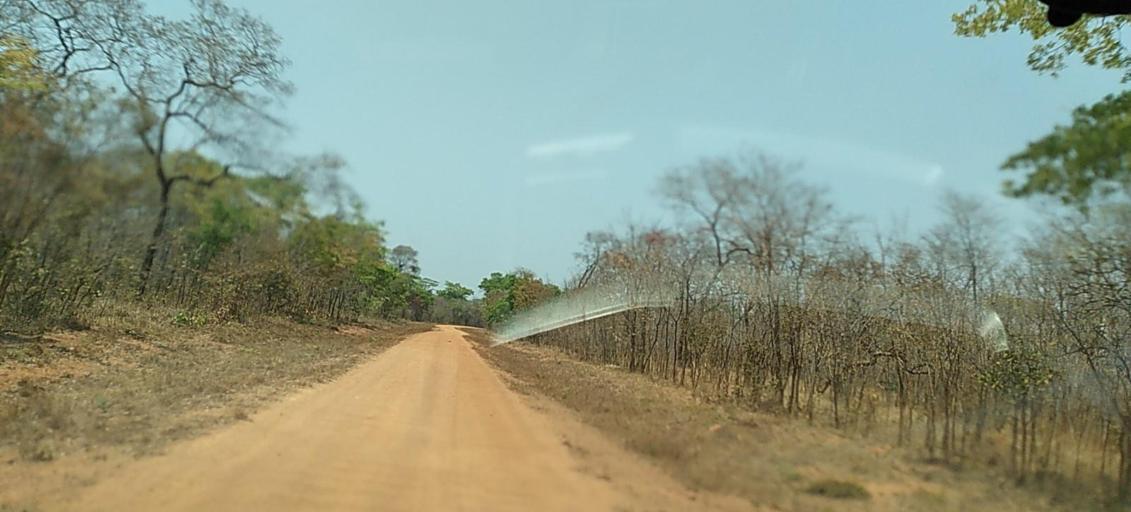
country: ZM
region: Central
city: Mumbwa
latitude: -14.3851
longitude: 26.4849
